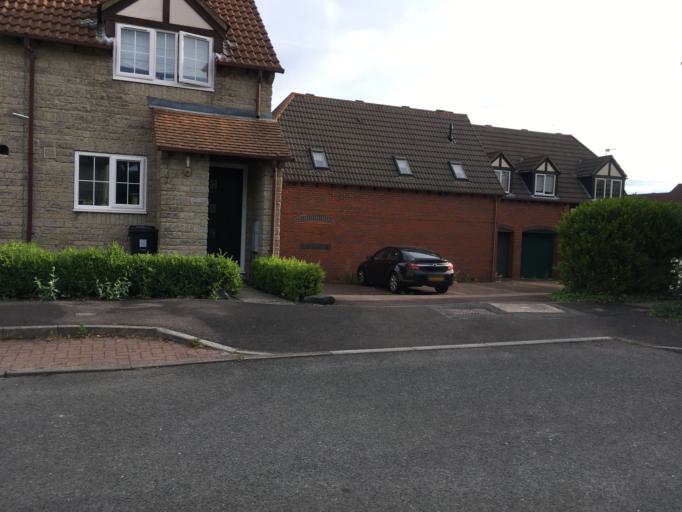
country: GB
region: England
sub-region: South Gloucestershire
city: Almondsbury
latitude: 51.5397
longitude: -2.5573
